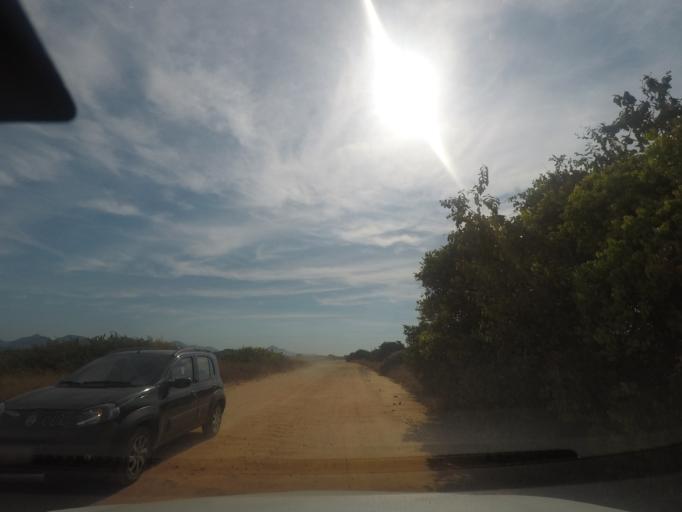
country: BR
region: Rio de Janeiro
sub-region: Marica
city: Marica
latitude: -22.9603
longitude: -42.8475
